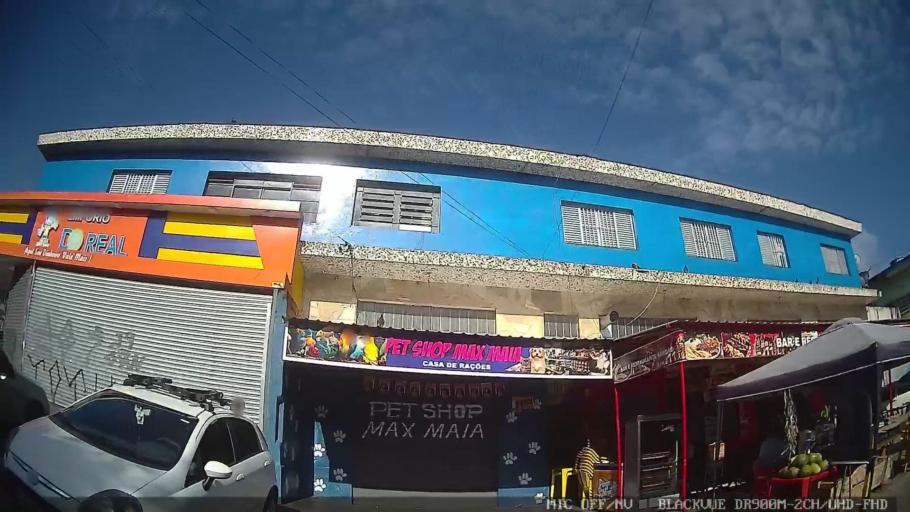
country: BR
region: Sao Paulo
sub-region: Itaquaquecetuba
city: Itaquaquecetuba
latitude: -23.4934
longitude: -46.4023
